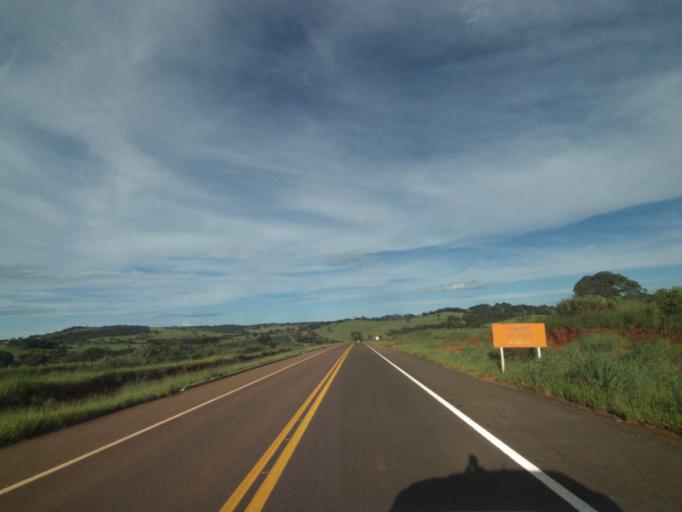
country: BR
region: Goias
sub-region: Jaragua
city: Jaragua
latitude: -15.9006
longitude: -49.5307
